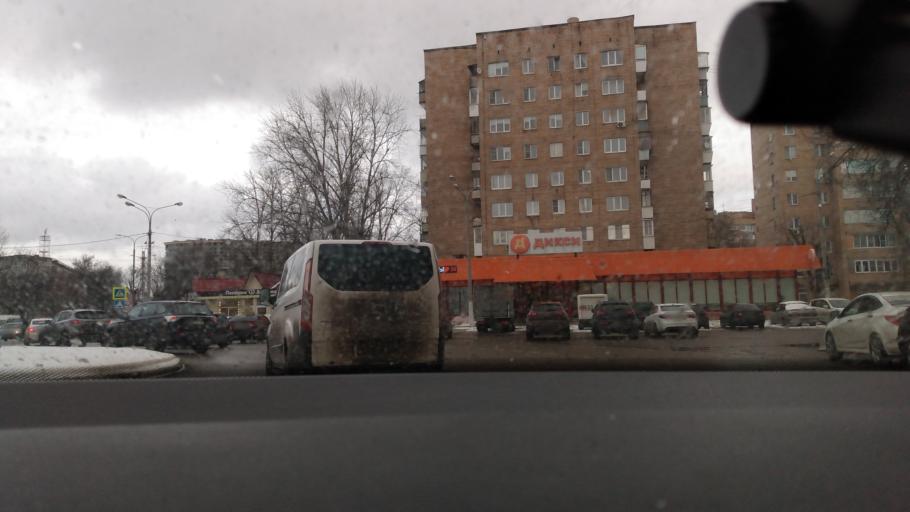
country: RU
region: Moskovskaya
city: Shchelkovo
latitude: 55.9159
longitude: 37.9906
